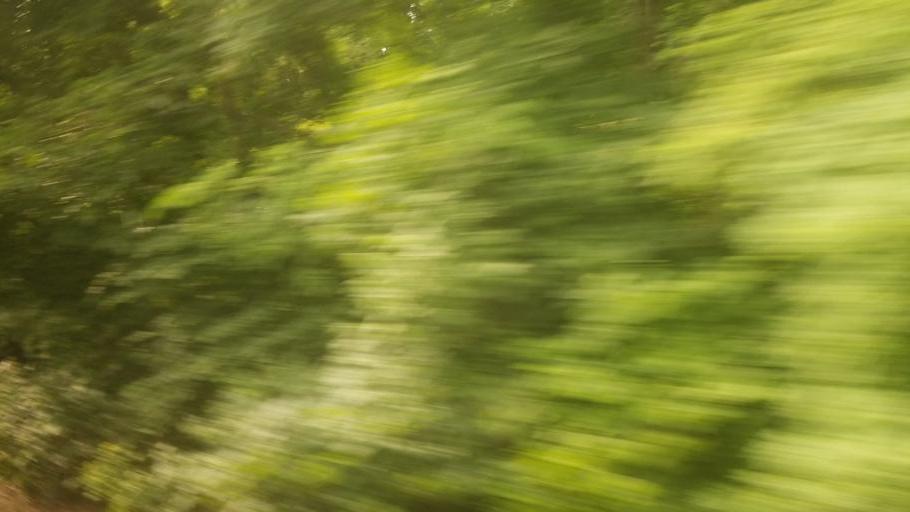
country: US
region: Kansas
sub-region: Douglas County
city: Lawrence
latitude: 39.0306
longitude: -95.3408
